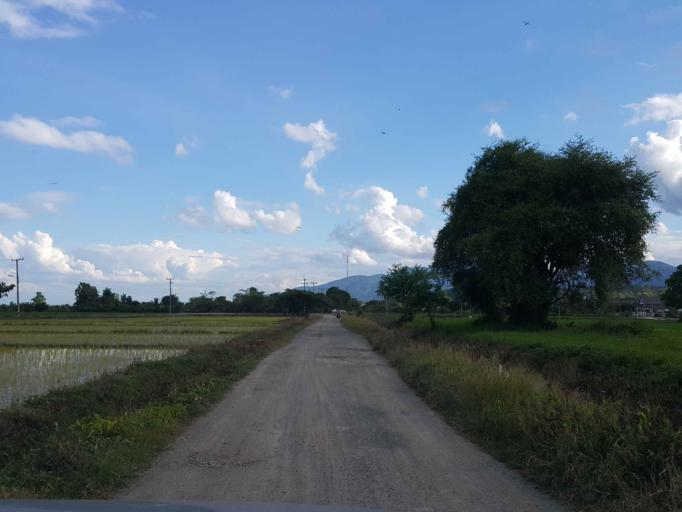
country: TH
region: Chiang Mai
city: Mae Taeng
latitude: 18.9911
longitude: 98.9492
